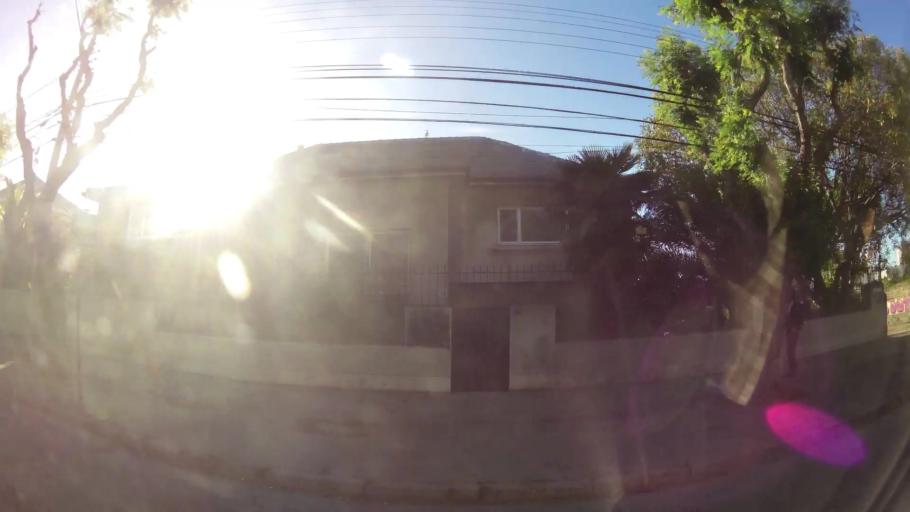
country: CL
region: Valparaiso
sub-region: Provincia de Valparaiso
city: Vina del Mar
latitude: -33.0303
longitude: -71.5812
